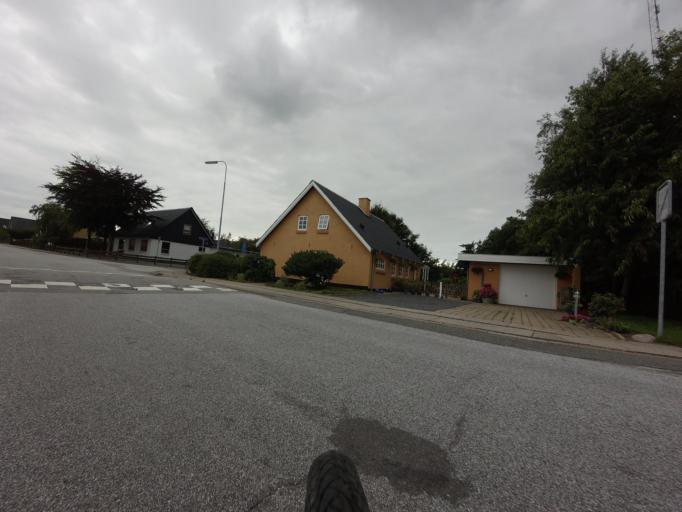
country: DK
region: North Denmark
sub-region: Hjorring Kommune
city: Hirtshals
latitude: 57.5630
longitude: 10.0292
